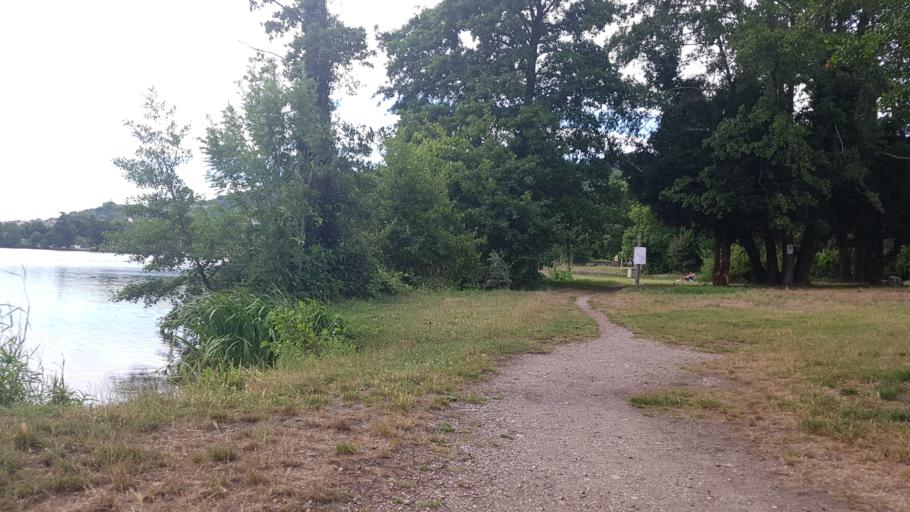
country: FR
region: Lorraine
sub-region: Departement de Meurthe-et-Moselle
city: Messein
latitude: 48.6072
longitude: 6.1484
